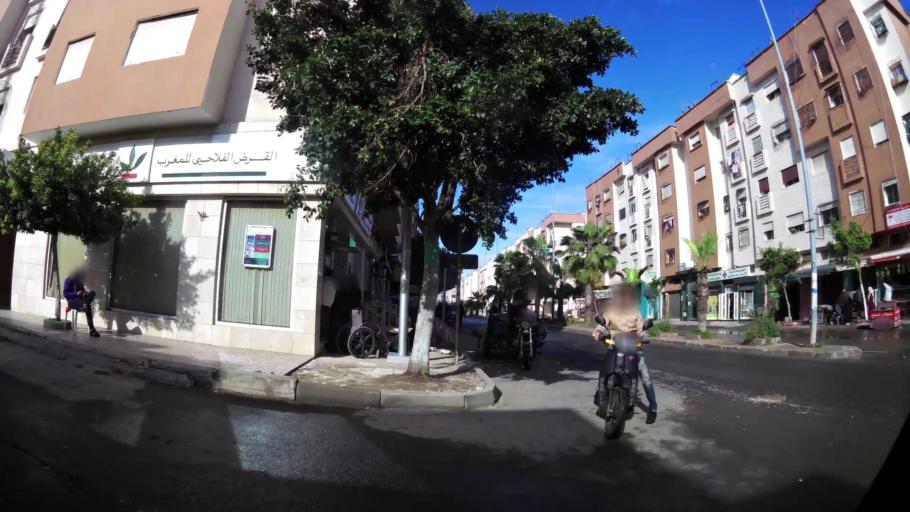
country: MA
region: Grand Casablanca
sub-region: Casablanca
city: Casablanca
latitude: 33.5543
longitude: -7.7004
